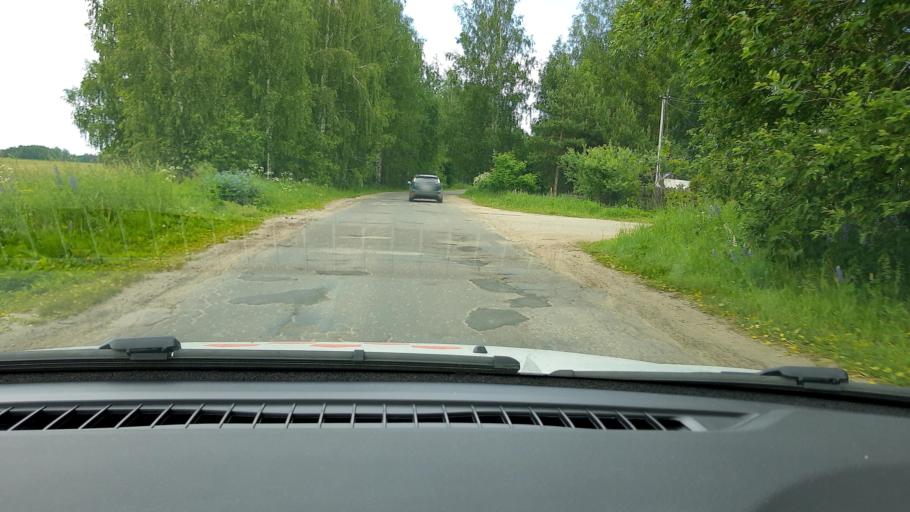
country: RU
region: Nizjnij Novgorod
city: Sitniki
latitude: 56.5305
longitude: 44.0966
